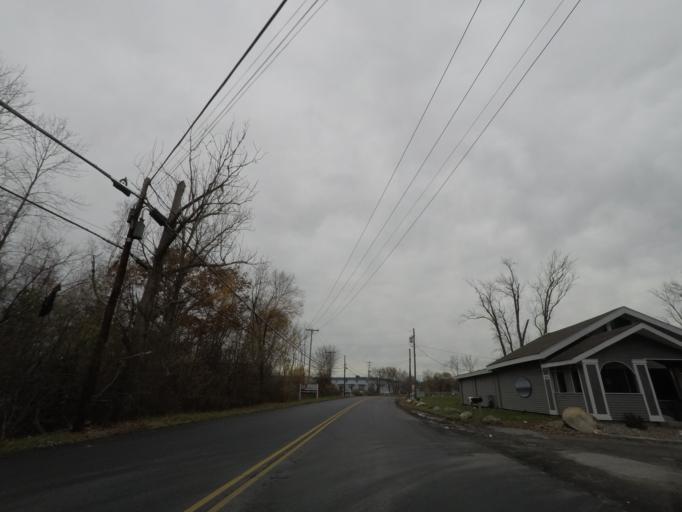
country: US
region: New York
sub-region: Saratoga County
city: Waterford
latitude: 42.8258
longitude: -73.6674
